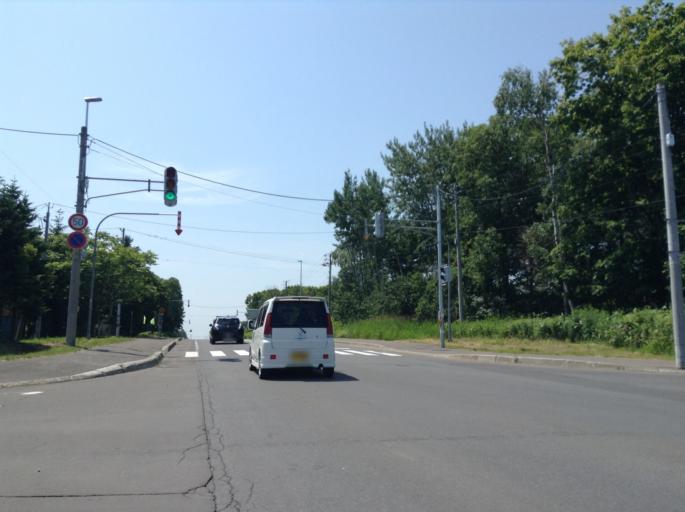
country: JP
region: Hokkaido
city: Nayoro
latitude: 44.3466
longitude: 142.4748
